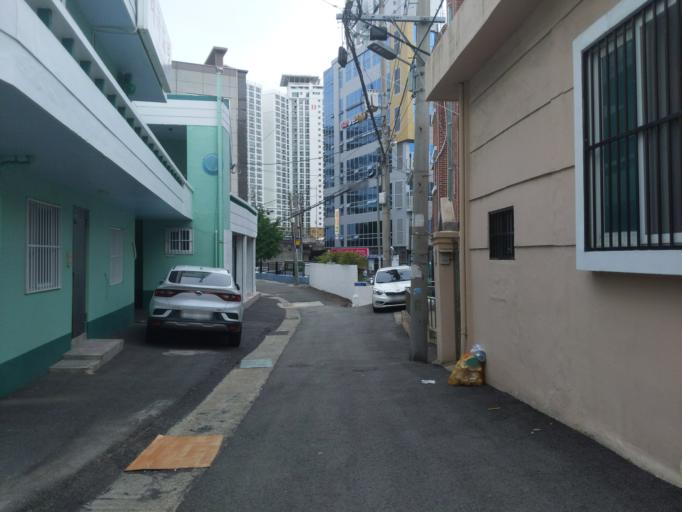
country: KR
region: Busan
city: Busan
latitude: 35.1596
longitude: 129.1288
